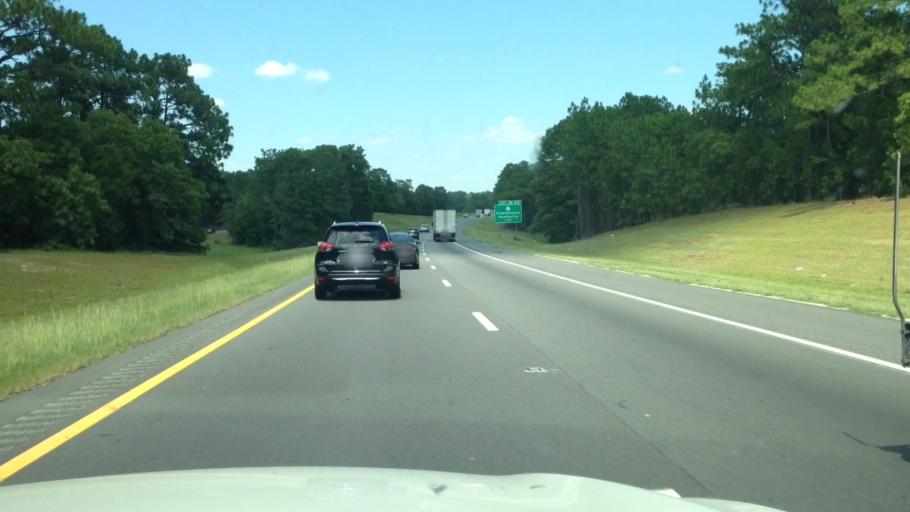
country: US
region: North Carolina
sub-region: Cumberland County
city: Hope Mills
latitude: 34.9667
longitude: -78.8823
